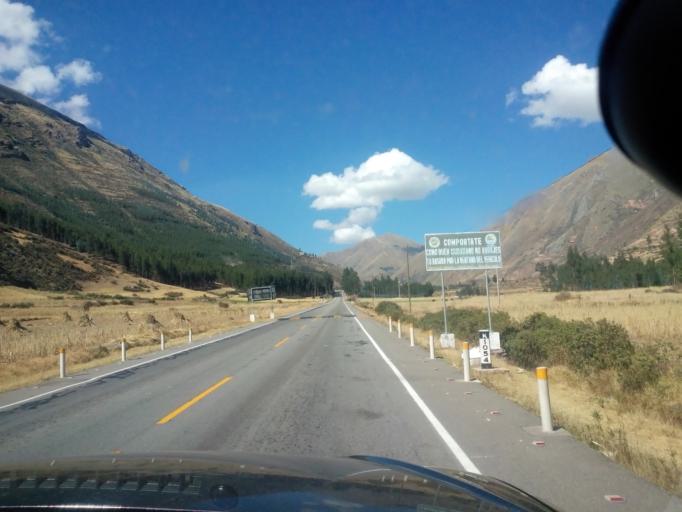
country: PE
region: Cusco
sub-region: Provincia de Quispicanchis
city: Cusipata
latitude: -13.9293
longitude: -71.5044
